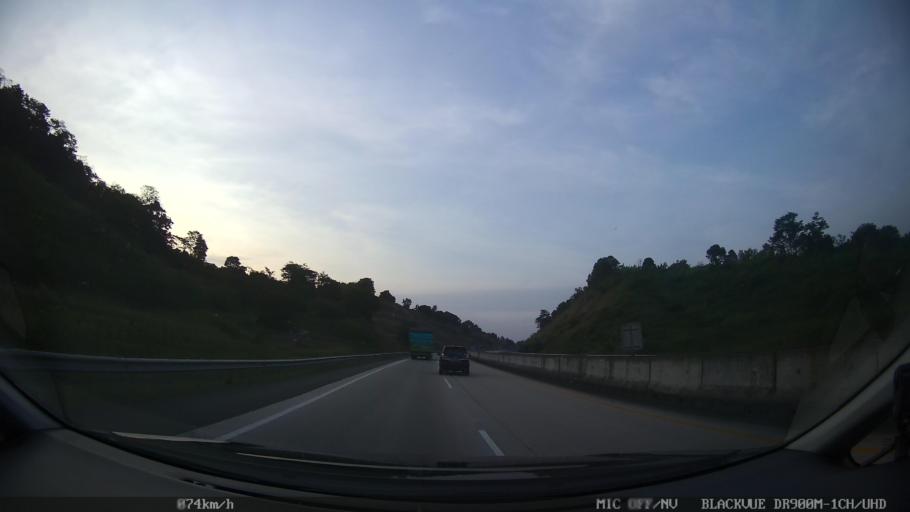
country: ID
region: Lampung
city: Penengahan
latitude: -5.8586
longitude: 105.7313
